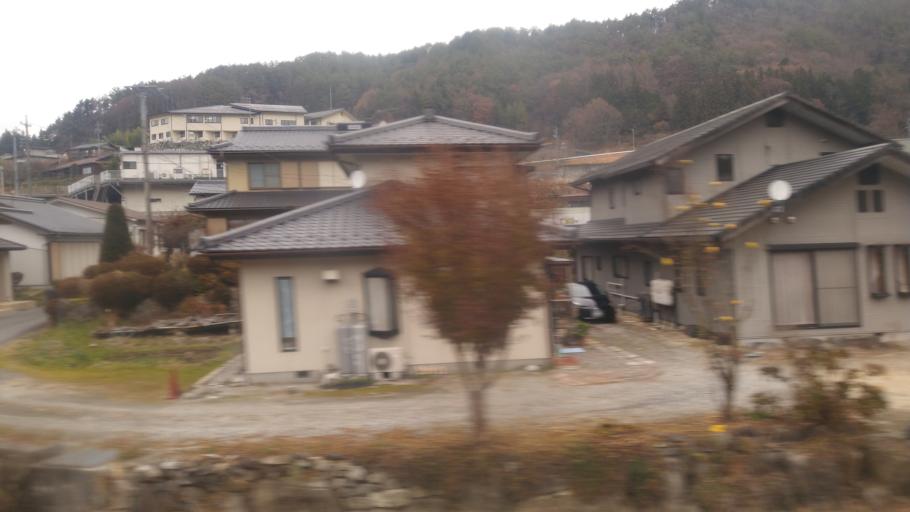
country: JP
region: Nagano
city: Ina
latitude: 35.7740
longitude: 137.6978
